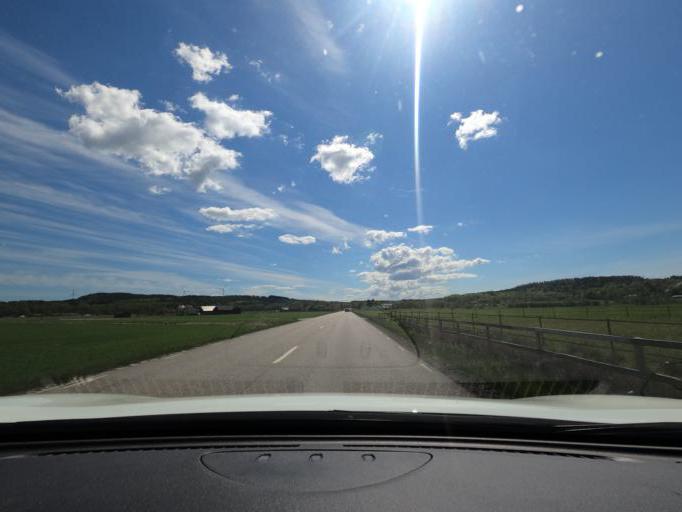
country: SE
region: Halland
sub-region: Kungsbacka Kommun
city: Fjaeras kyrkby
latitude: 57.4279
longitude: 12.1914
